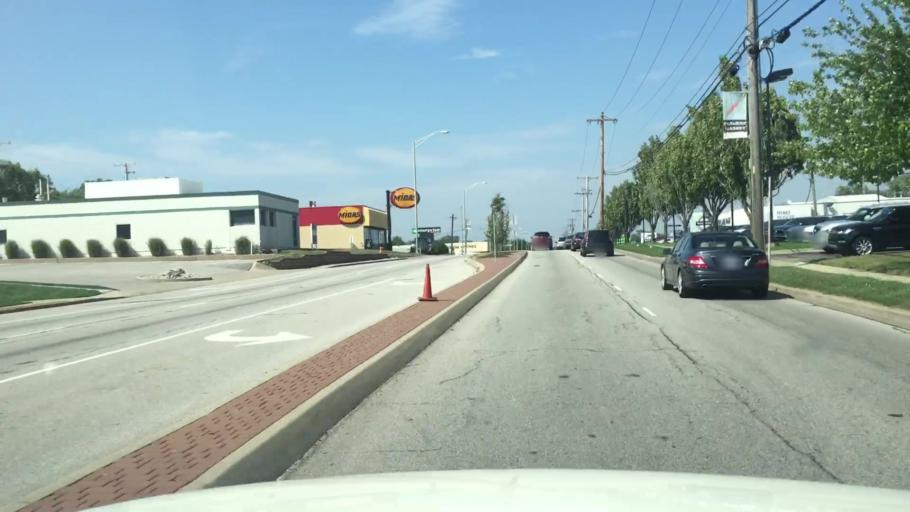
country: US
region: Kansas
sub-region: Johnson County
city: Overland Park
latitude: 38.9861
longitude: -94.6677
